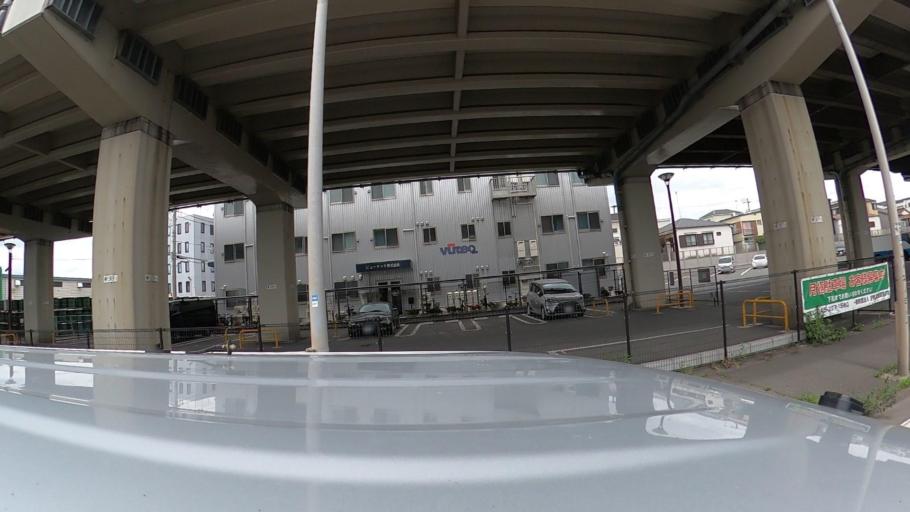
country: JP
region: Kanagawa
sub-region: Kawasaki-shi
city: Kawasaki
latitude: 35.4950
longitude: 139.6802
